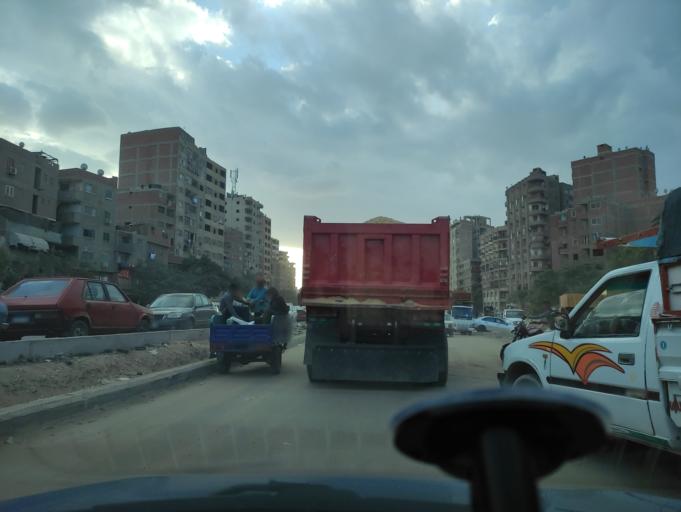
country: EG
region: Muhafazat al Qalyubiyah
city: Al Khankah
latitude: 30.1357
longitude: 31.3321
